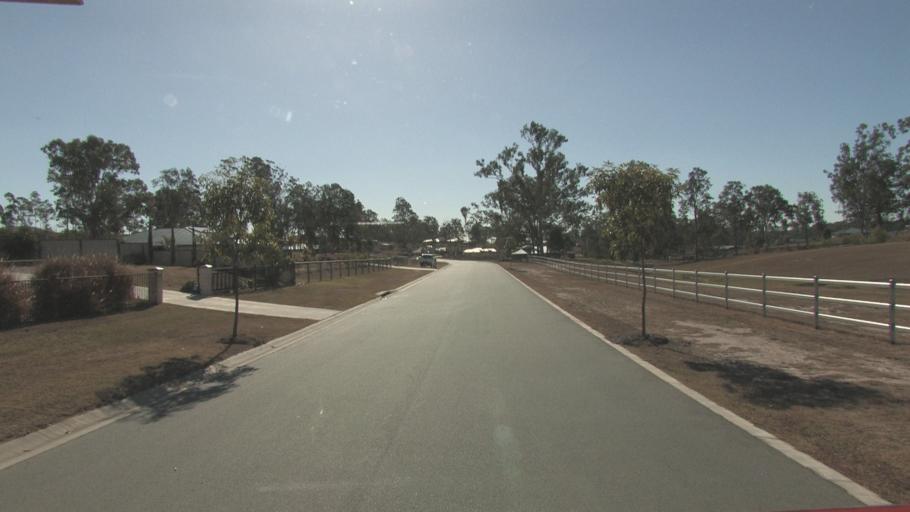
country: AU
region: Queensland
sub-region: Logan
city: Cedar Vale
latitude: -27.8711
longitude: 153.0561
